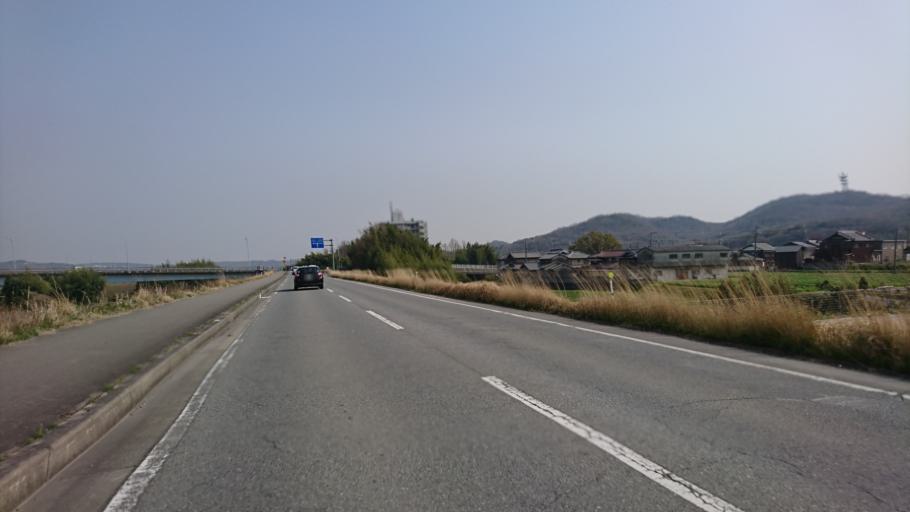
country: JP
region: Hyogo
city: Ono
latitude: 34.8372
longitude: 134.9182
